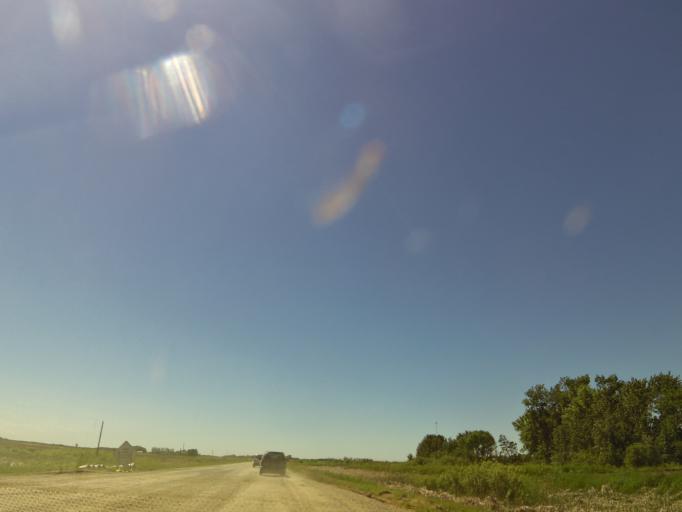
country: US
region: Minnesota
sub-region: Mahnomen County
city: Mahnomen
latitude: 47.3802
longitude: -95.9708
